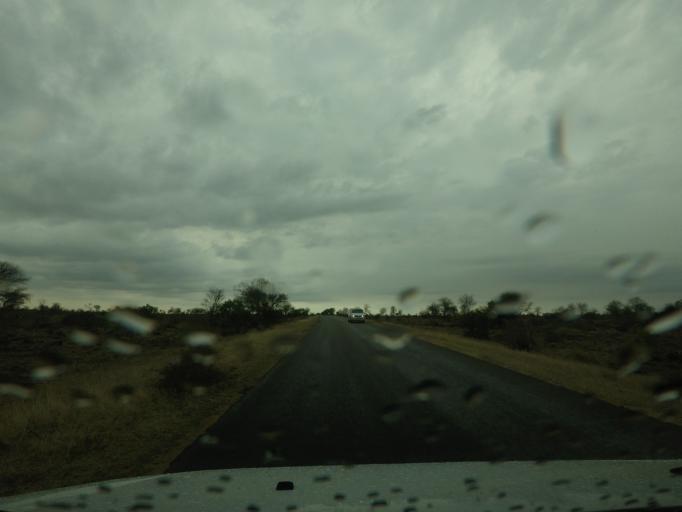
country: ZA
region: Limpopo
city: Thulamahashi
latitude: -24.4756
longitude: 31.3974
